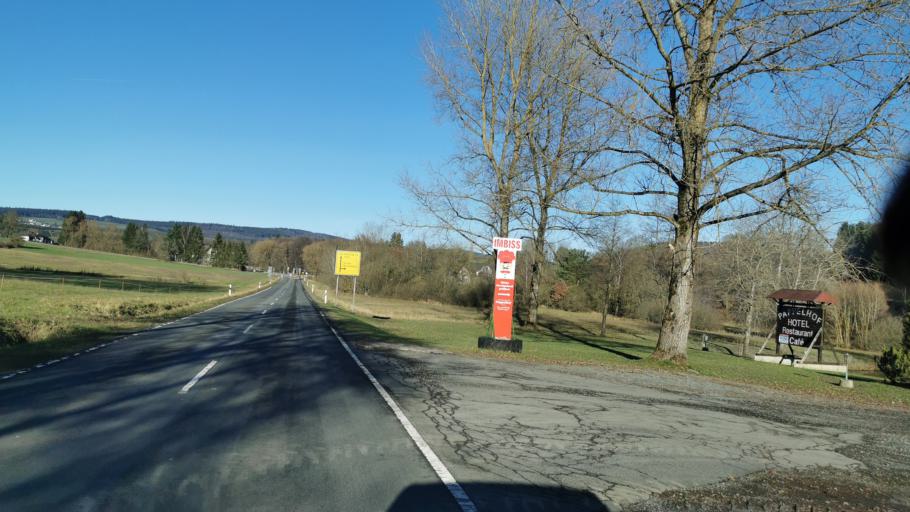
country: DE
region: Rheinland-Pfalz
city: Weidenbach
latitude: 50.1274
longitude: 6.7043
